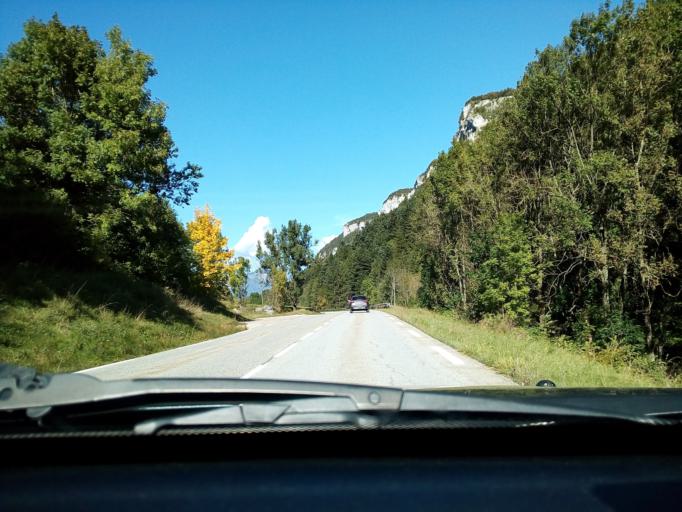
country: FR
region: Rhone-Alpes
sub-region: Departement de l'Isere
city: Lans-en-Vercors
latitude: 45.1641
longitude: 5.6101
